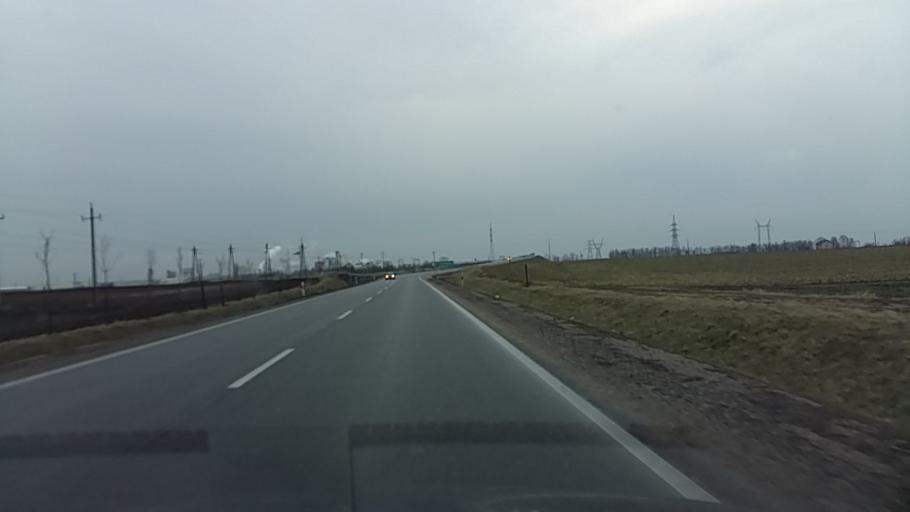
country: HU
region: Fejer
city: Sarosd
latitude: 47.0885
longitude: 18.6989
